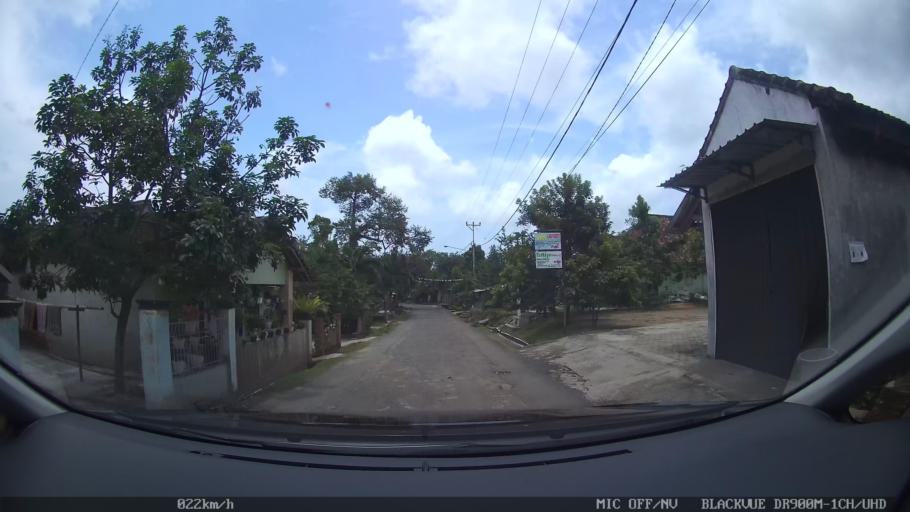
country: ID
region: Lampung
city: Bandarlampung
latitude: -5.4225
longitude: 105.2295
